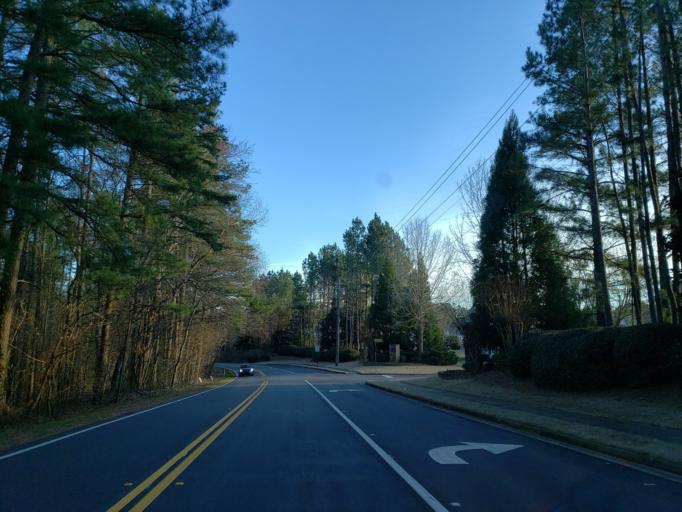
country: US
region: Georgia
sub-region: Cobb County
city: Acworth
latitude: 34.0341
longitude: -84.7275
